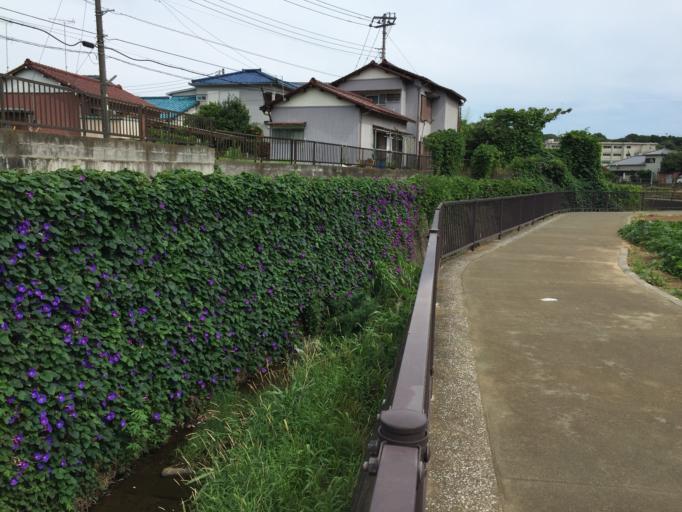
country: JP
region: Kanagawa
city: Miura
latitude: 35.2030
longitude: 139.6617
